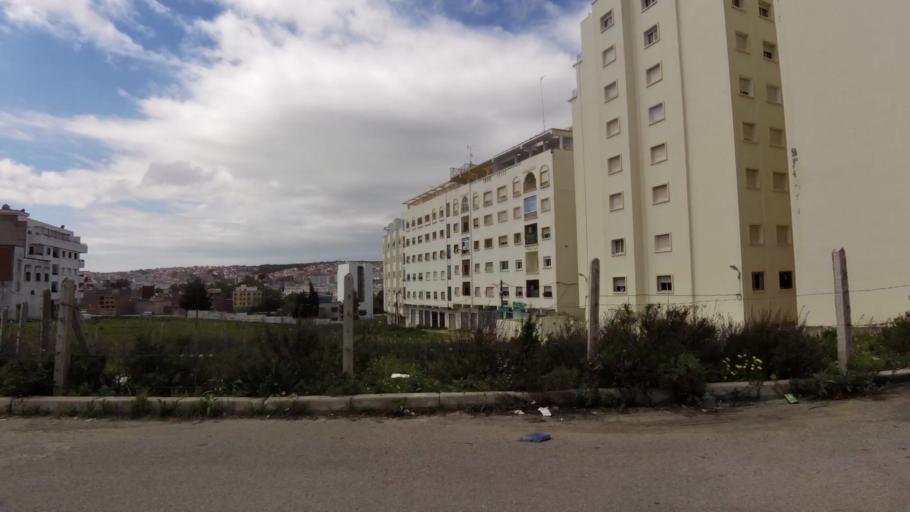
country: MA
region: Tanger-Tetouan
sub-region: Tanger-Assilah
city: Tangier
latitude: 35.7668
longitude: -5.8432
